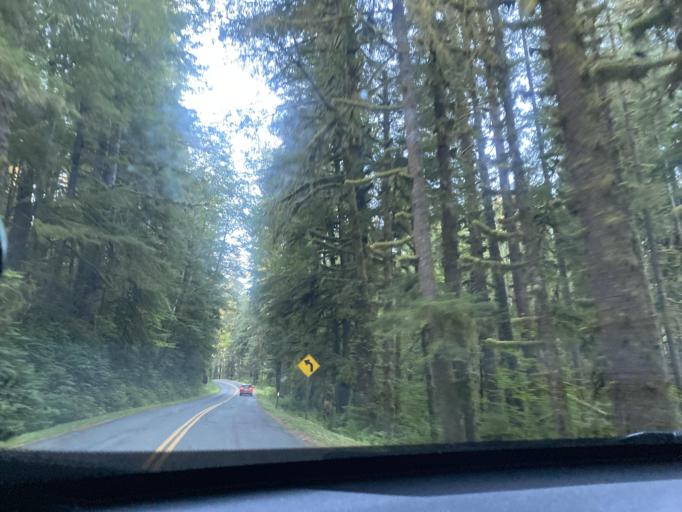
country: US
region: Washington
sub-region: Clallam County
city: Forks
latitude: 47.8115
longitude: -124.1033
